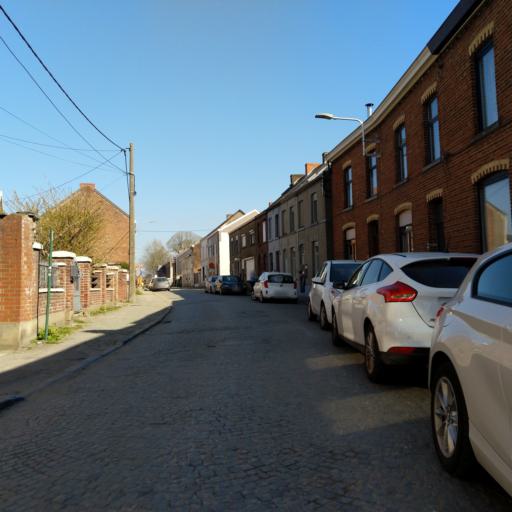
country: BE
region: Wallonia
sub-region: Province du Hainaut
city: Mons
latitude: 50.4701
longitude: 3.9595
